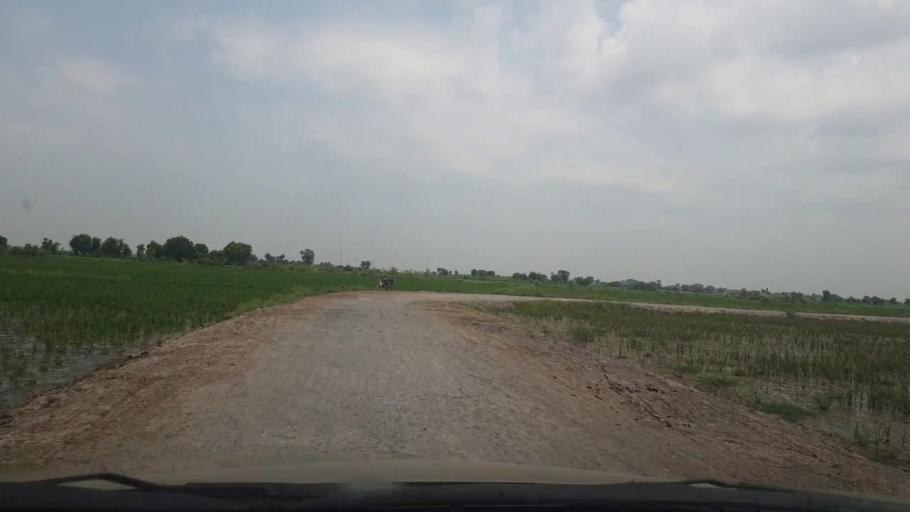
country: PK
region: Sindh
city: Ratodero
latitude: 27.7151
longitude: 68.2282
